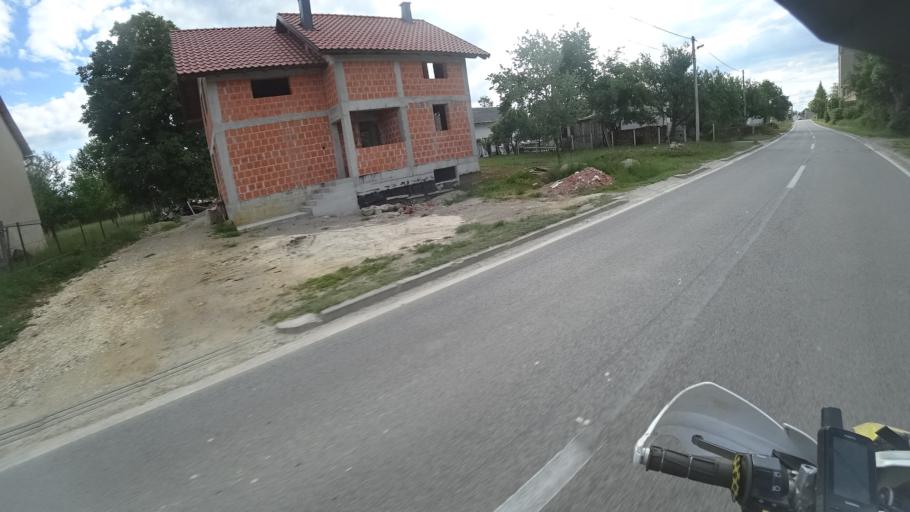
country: HR
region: Licko-Senjska
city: Gospic
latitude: 44.5326
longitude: 15.3990
